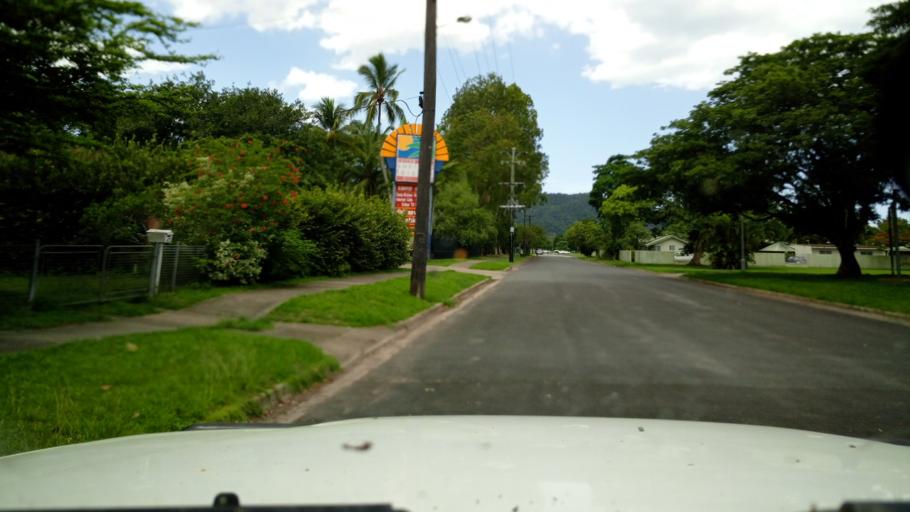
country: AU
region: Queensland
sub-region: Cairns
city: Cairns
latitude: -16.9182
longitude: 145.7405
